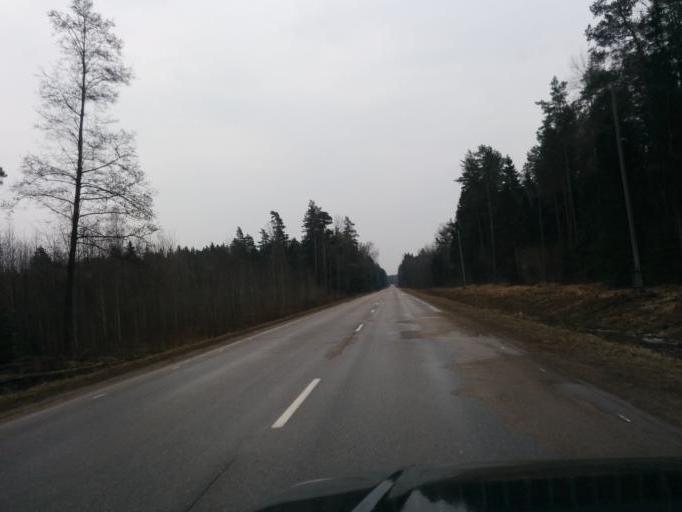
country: LV
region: Ikskile
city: Ikskile
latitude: 56.8124
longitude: 24.4794
